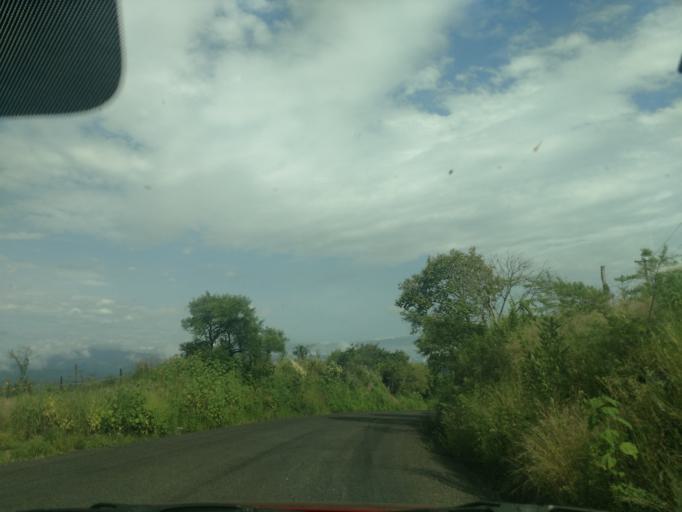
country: MX
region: Jalisco
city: El Salto
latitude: 20.4336
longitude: -104.4528
